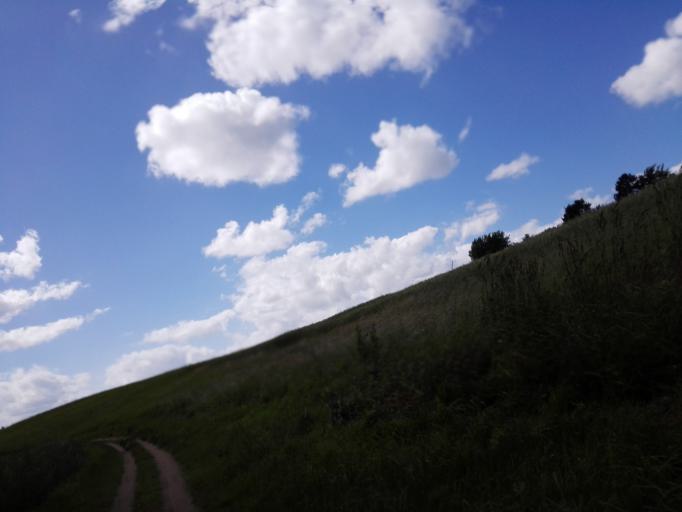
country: DK
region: Capital Region
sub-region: Allerod Kommune
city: Lynge
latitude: 55.8212
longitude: 12.2829
